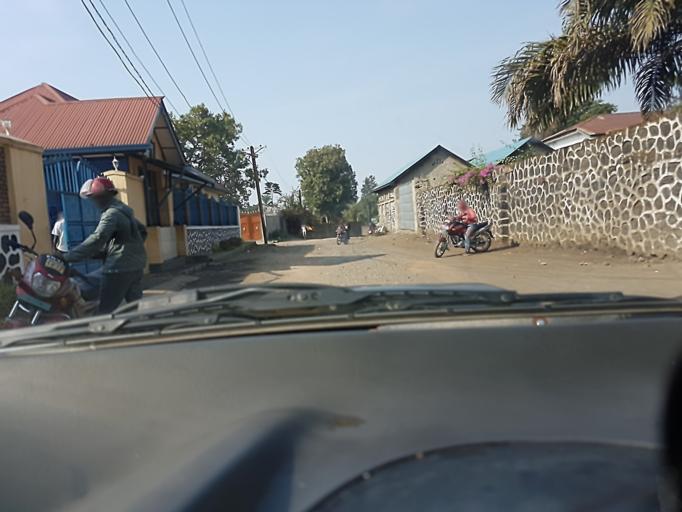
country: RW
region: Western Province
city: Gisenyi
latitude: -1.6969
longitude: 29.2388
